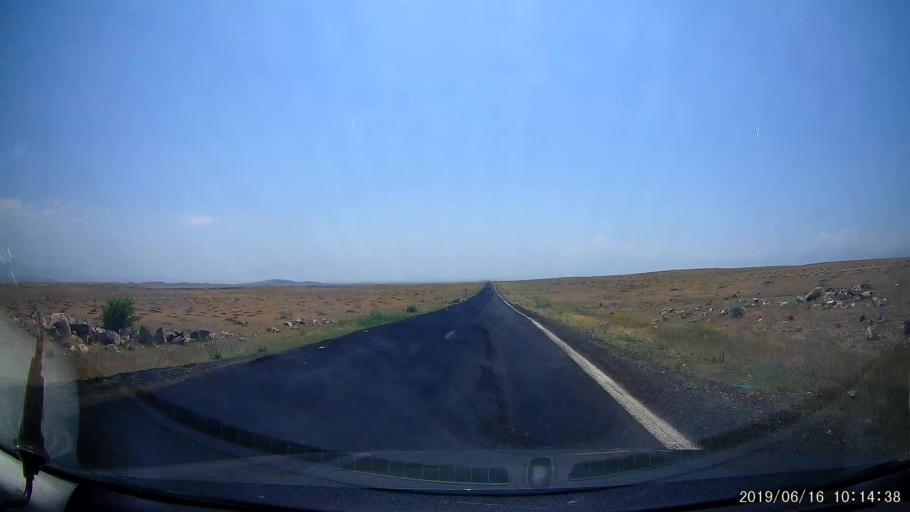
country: TR
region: Igdir
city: Tuzluca
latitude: 40.1831
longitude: 43.6668
